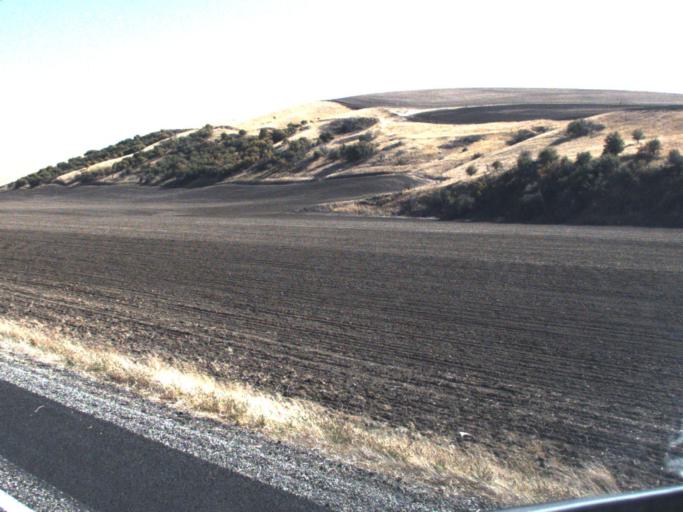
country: US
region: Washington
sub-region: Walla Walla County
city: Waitsburg
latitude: 46.2666
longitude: -118.2032
